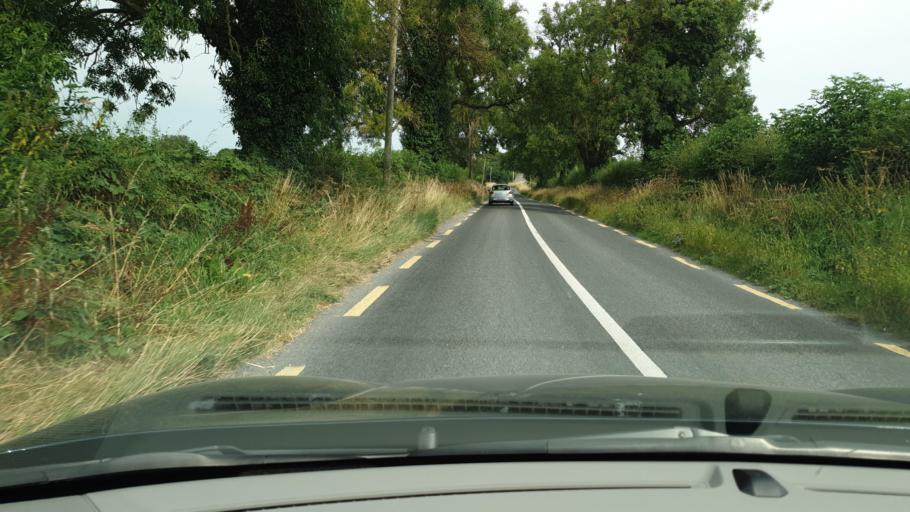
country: IE
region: Leinster
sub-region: An Mhi
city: Athboy
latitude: 53.6575
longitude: -6.8954
